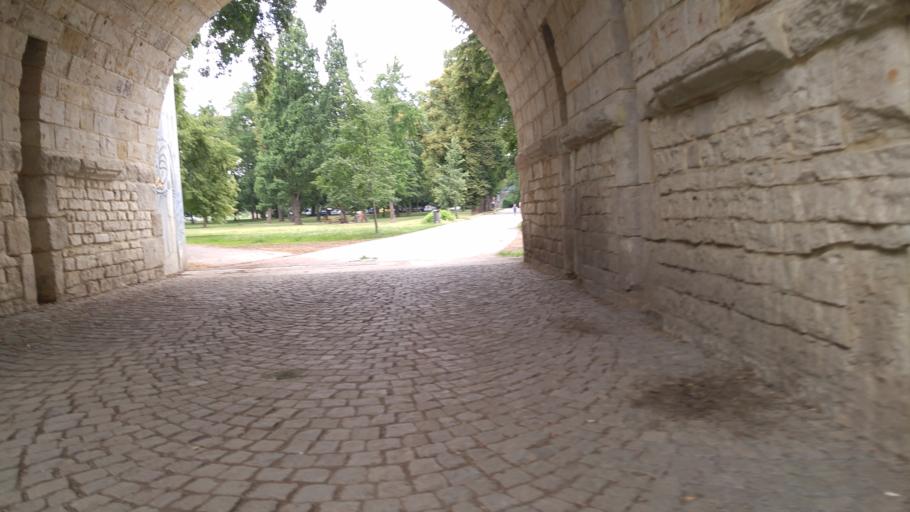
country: CZ
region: Praha
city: Prague
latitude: 50.1094
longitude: 14.4186
